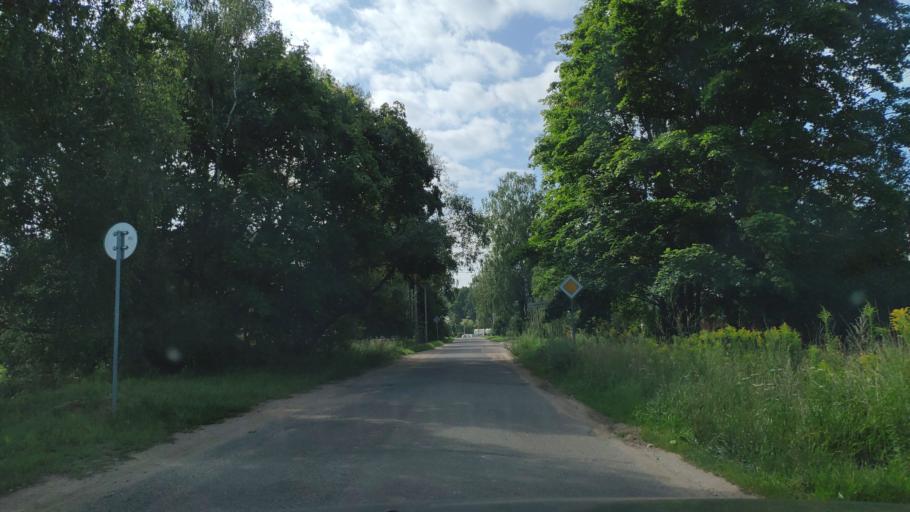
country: BY
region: Minsk
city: Zaslawye
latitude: 53.9923
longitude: 27.2844
